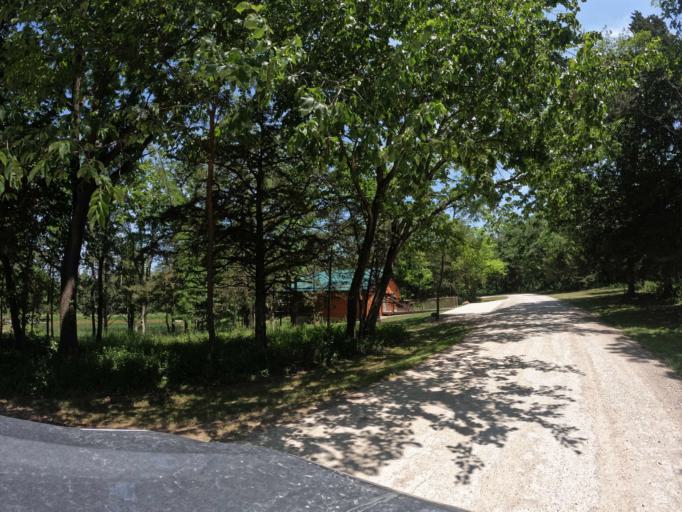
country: US
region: Iowa
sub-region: Henry County
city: Mount Pleasant
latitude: 40.9309
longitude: -91.6167
